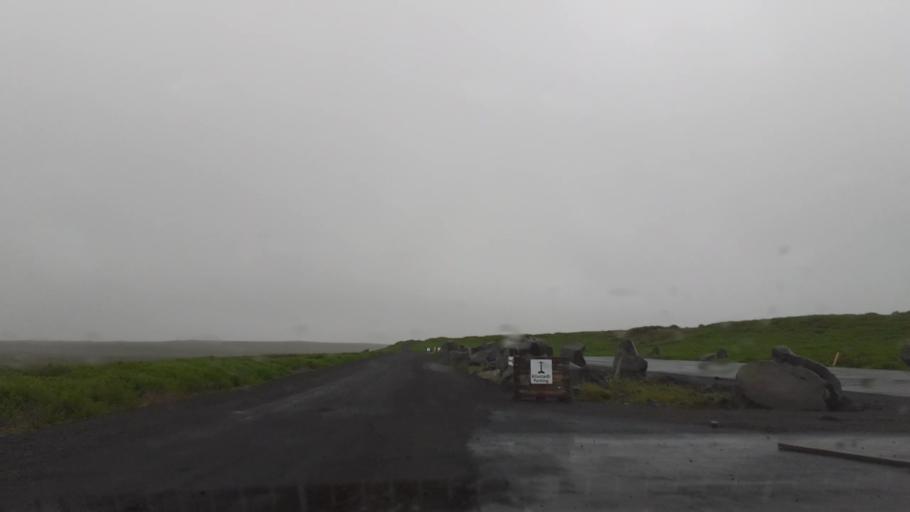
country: IS
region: Northeast
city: Husavik
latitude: 66.4609
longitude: -15.9592
